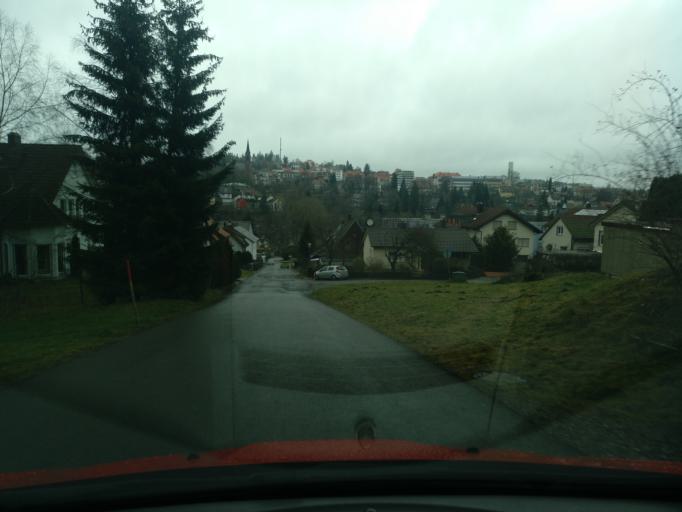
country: DE
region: Baden-Wuerttemberg
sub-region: Freiburg Region
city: Sankt Georgen im Schwarzwald
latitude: 48.1186
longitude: 8.3329
